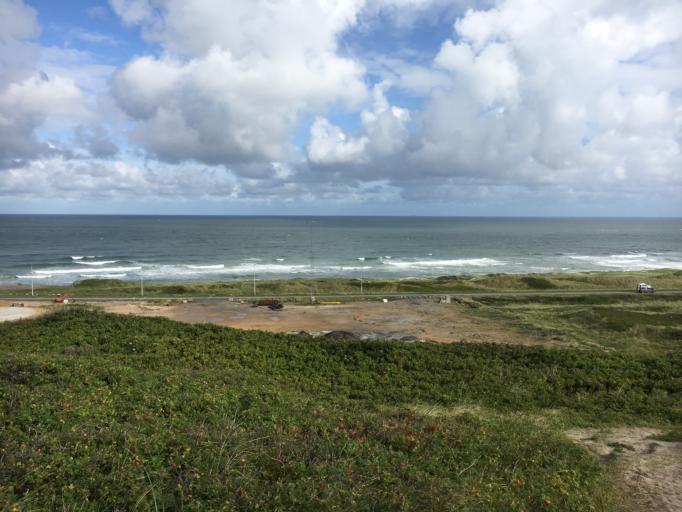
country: DK
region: North Denmark
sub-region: Thisted Kommune
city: Hanstholm
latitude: 57.1223
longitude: 8.6150
